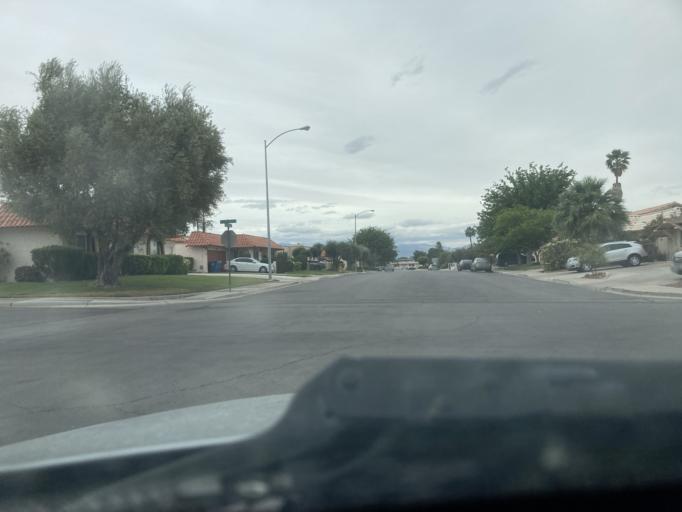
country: US
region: Nevada
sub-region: Clark County
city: Winchester
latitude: 36.1231
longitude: -115.0998
